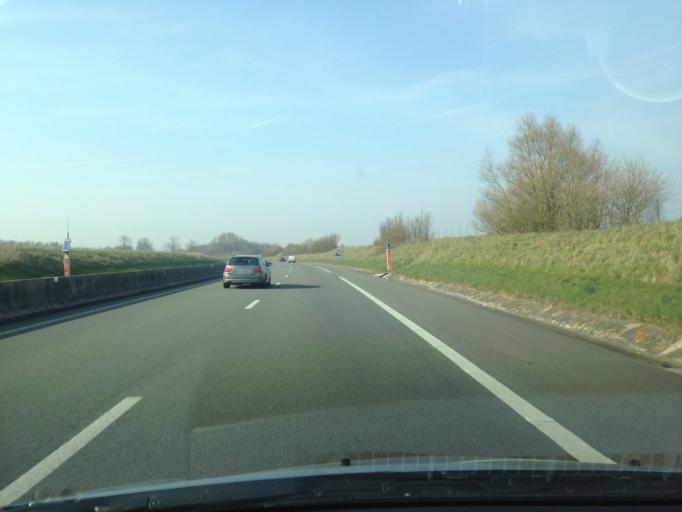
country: FR
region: Nord-Pas-de-Calais
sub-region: Departement du Pas-de-Calais
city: Saint-Josse
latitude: 50.4687
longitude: 1.7033
